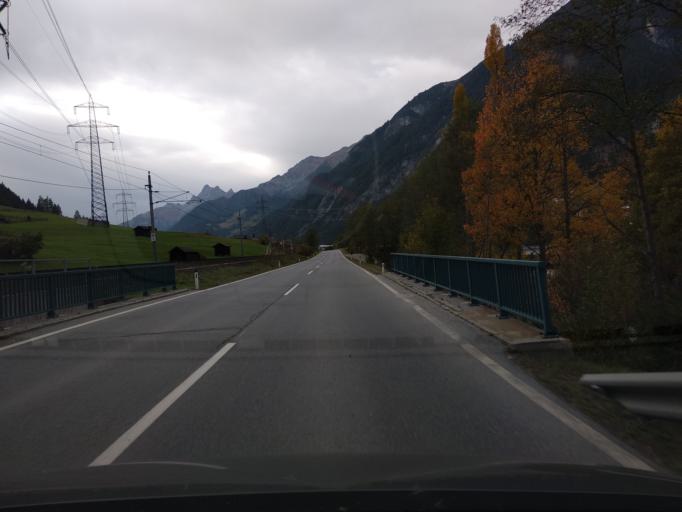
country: AT
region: Tyrol
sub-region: Politischer Bezirk Landeck
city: Flirsch
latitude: 47.1493
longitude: 10.3881
